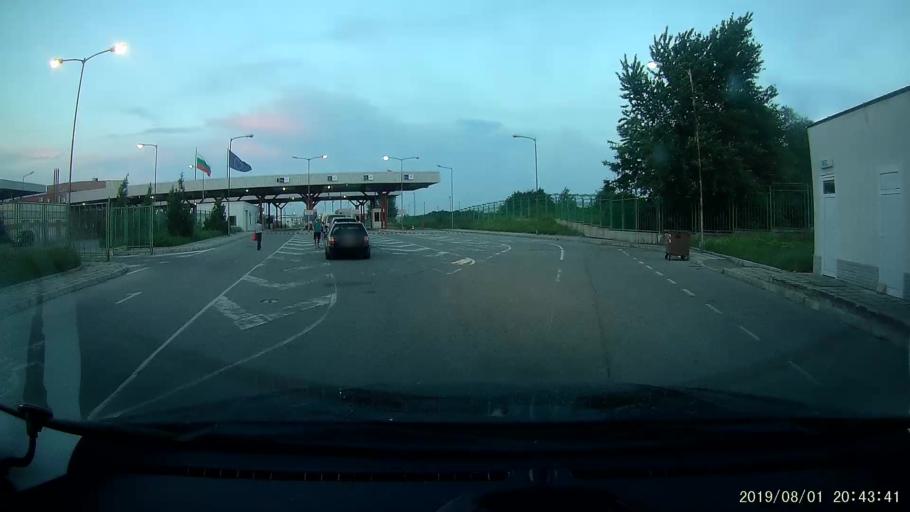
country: TR
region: Edirne
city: Lalapasa
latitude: 41.9616
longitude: 26.6043
